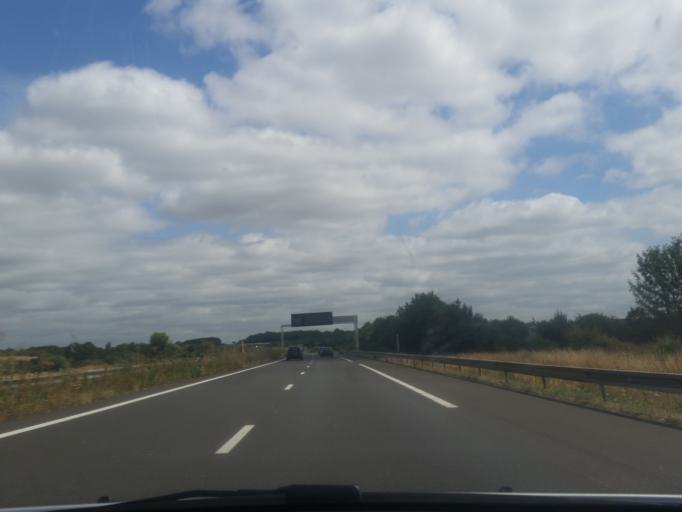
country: FR
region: Pays de la Loire
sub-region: Departement de Maine-et-Loire
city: Saint-Leger-des-Bois
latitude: 47.4515
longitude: -0.7126
